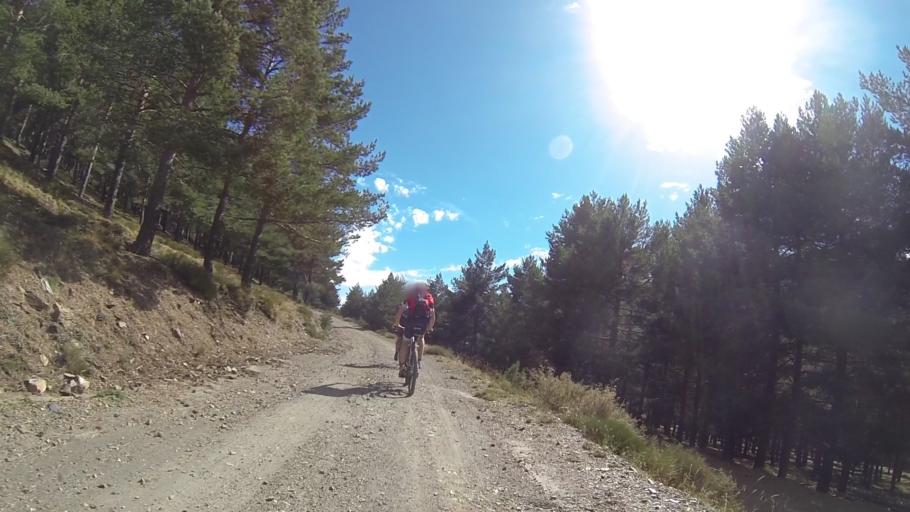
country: ES
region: Andalusia
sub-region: Provincia de Granada
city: Ferreira
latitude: 37.1117
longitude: -3.0269
